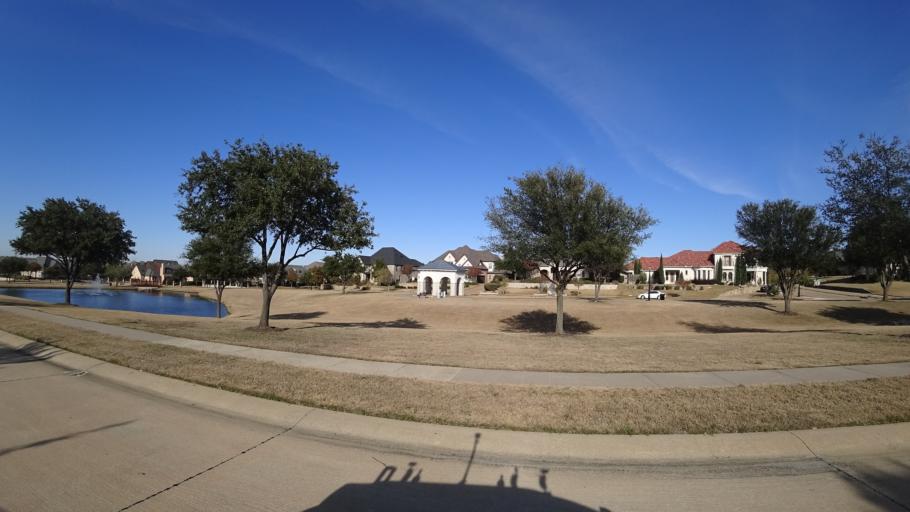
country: US
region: Texas
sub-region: Denton County
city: The Colony
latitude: 33.0393
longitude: -96.8972
